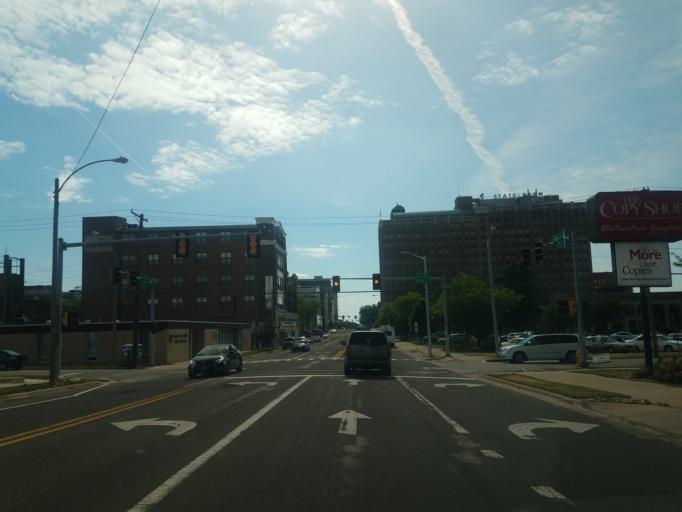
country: US
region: Illinois
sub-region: McLean County
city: Bloomington
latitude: 40.4797
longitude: -88.9905
